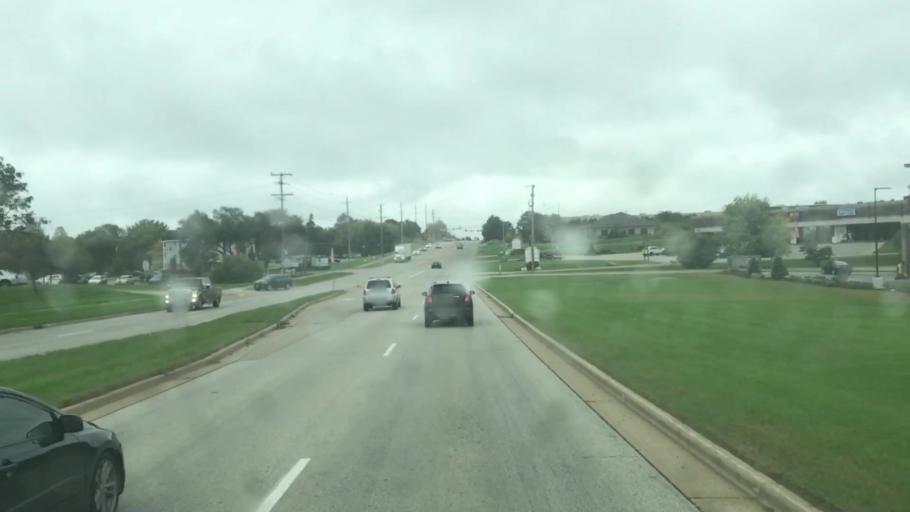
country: US
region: Wisconsin
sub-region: Waukesha County
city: Waukesha
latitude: 43.0365
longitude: -88.1803
